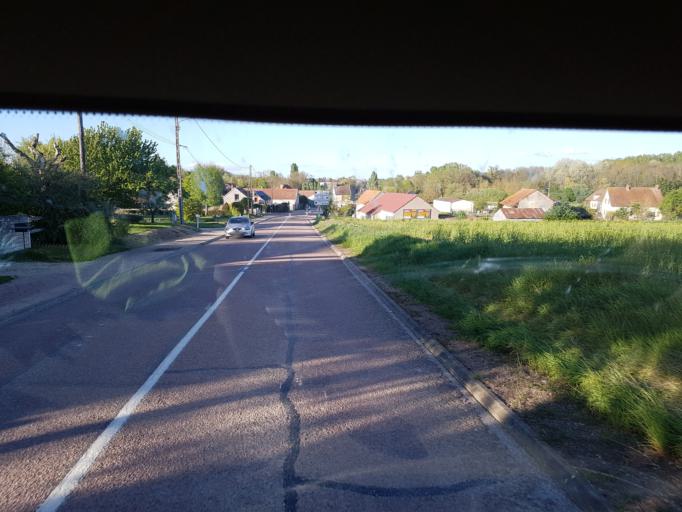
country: FR
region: Champagne-Ardenne
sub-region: Departement de l'Aube
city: Marigny-le-Chatel
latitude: 48.4344
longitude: 3.6734
